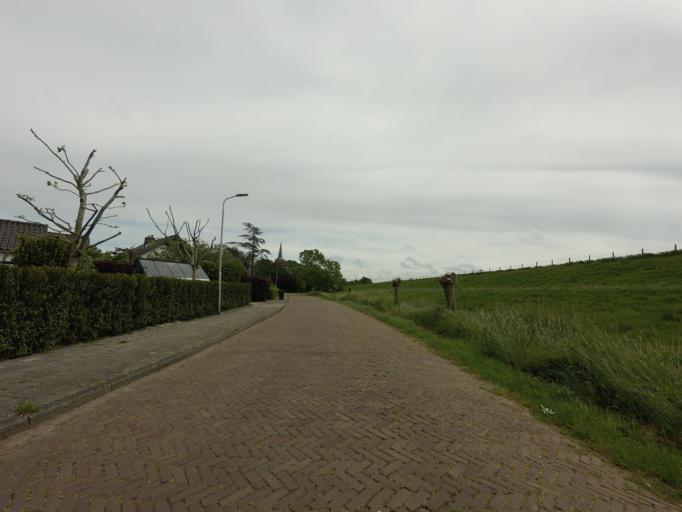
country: NL
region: North Holland
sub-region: Gemeente Hoorn
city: Hoorn
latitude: 52.6356
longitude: 5.1189
